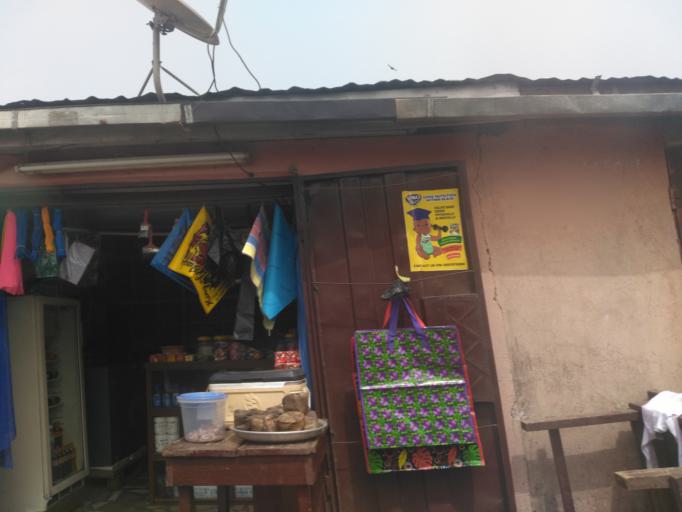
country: GH
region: Ashanti
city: Kumasi
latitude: 6.7009
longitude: -1.6113
